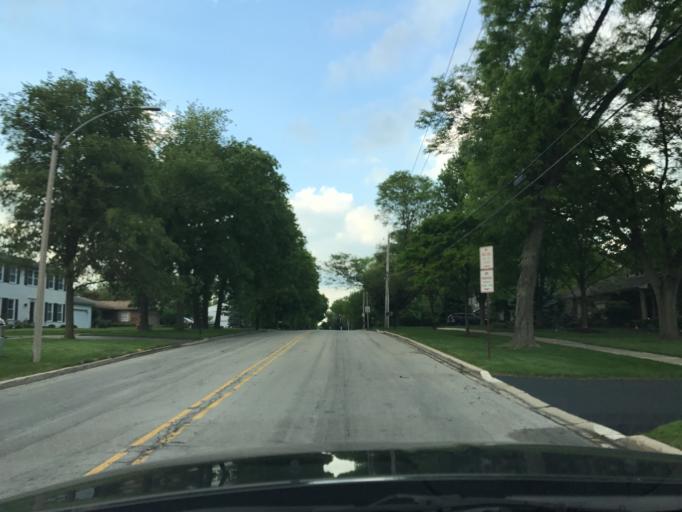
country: US
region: Illinois
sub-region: DuPage County
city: Naperville
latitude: 41.7667
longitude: -88.1207
